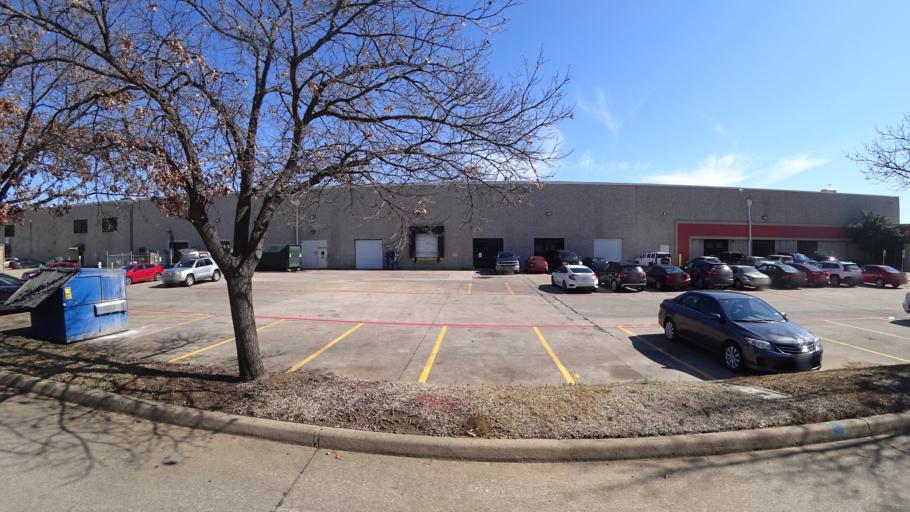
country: US
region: Texas
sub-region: Denton County
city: Lewisville
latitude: 33.0255
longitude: -96.9825
